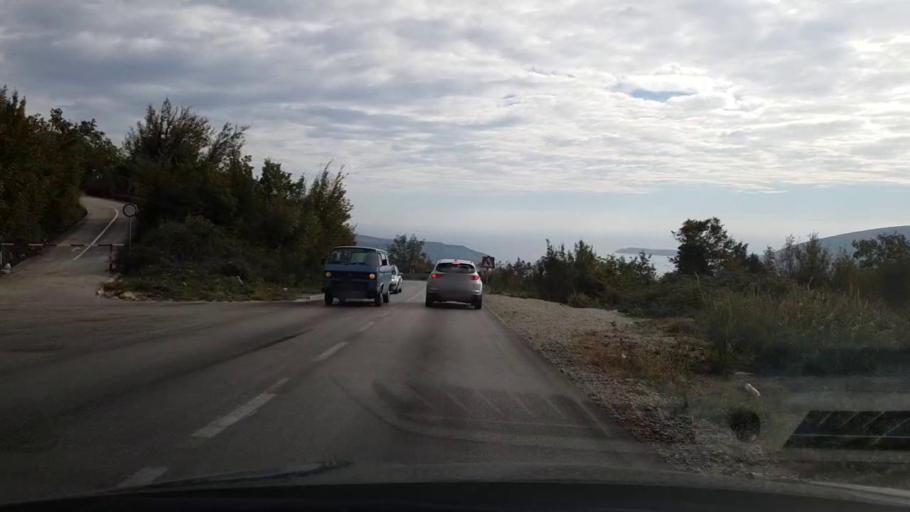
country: ME
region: Herceg Novi
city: Herceg-Novi
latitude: 42.4707
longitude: 18.5373
